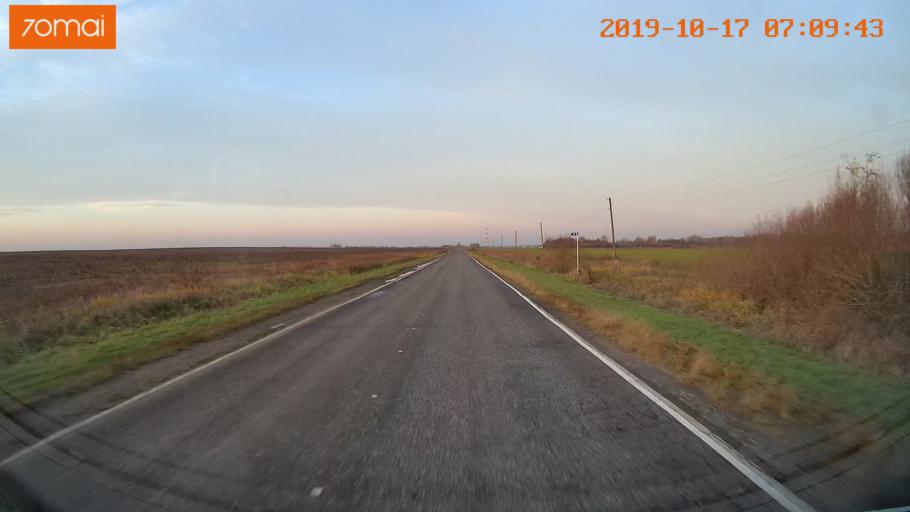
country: RU
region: Vladimir
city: Suzdal'
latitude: 56.4167
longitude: 40.3774
